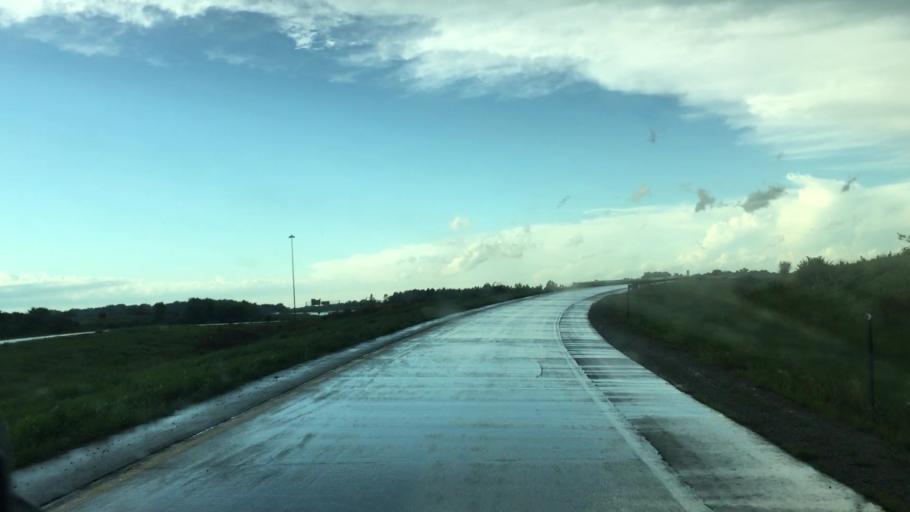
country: US
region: Iowa
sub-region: Henry County
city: Mount Pleasant
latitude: 40.9927
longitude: -91.5448
